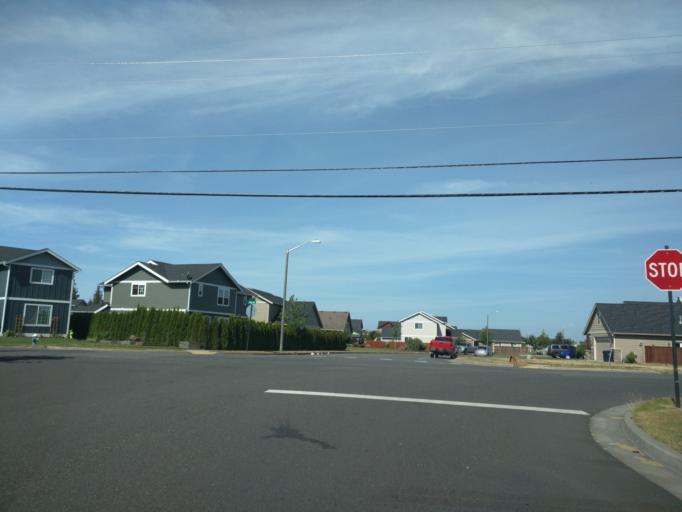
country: US
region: Washington
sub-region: Whatcom County
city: Lynden
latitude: 48.9618
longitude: -122.4184
